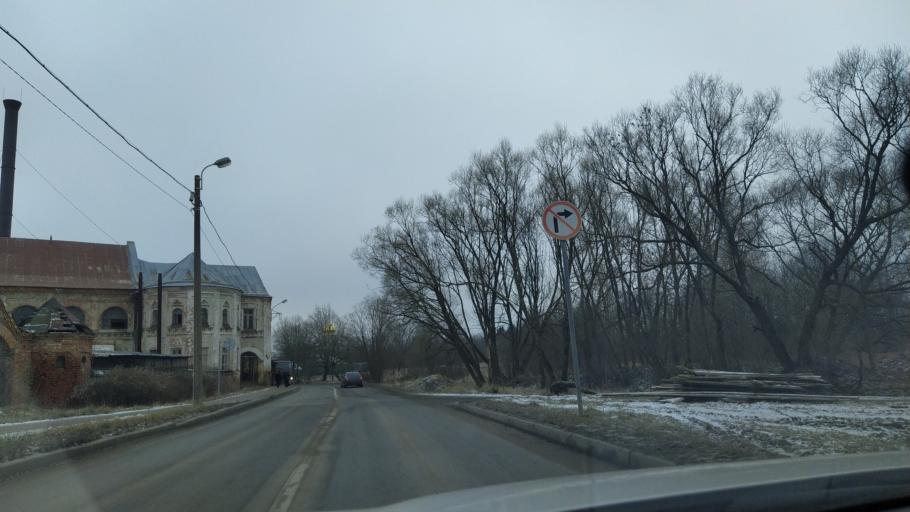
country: RU
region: St.-Petersburg
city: Pushkin
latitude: 59.7294
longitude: 30.3859
